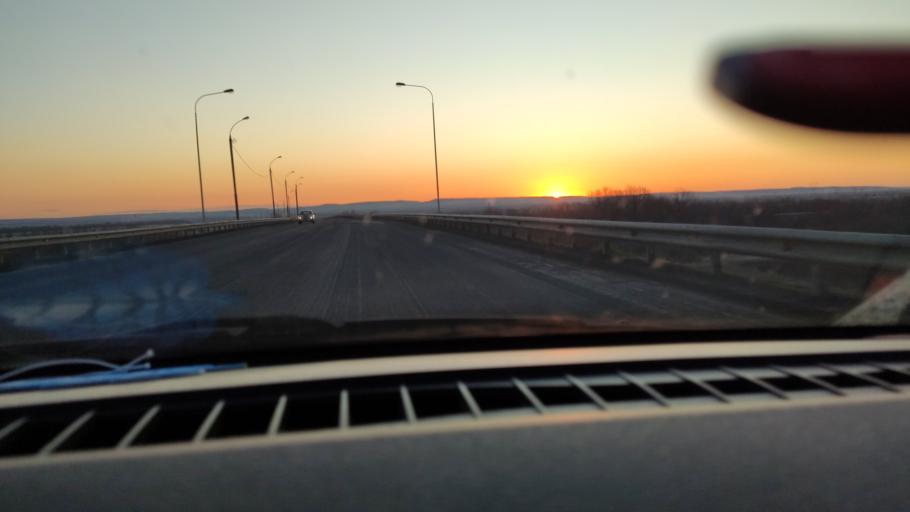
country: RU
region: Saratov
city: Yelshanka
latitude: 51.7994
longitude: 46.1841
